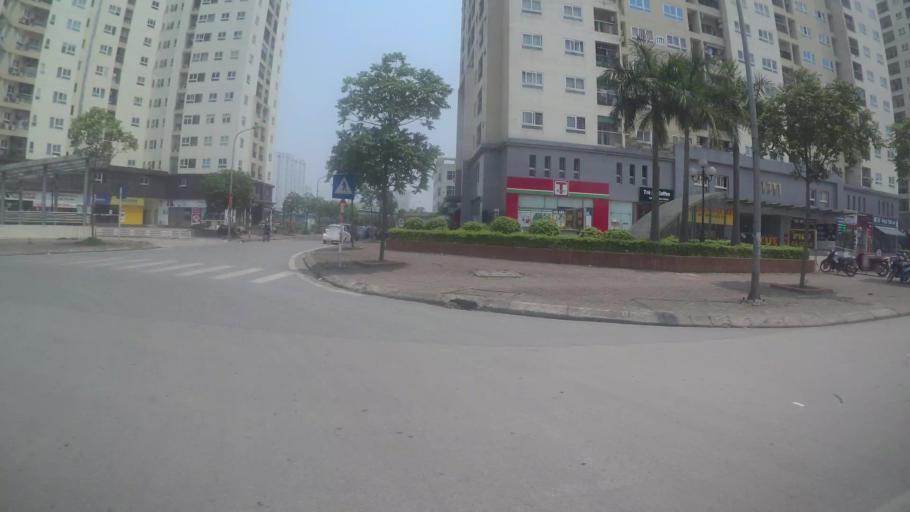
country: VN
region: Ha Noi
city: Thanh Xuan
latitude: 20.9952
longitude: 105.7785
